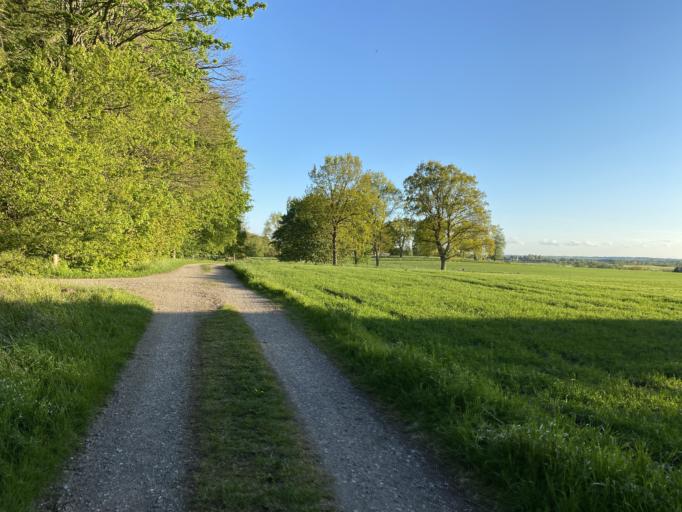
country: DK
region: Capital Region
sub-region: Fureso Kommune
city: Farum
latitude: 55.7946
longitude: 12.3451
